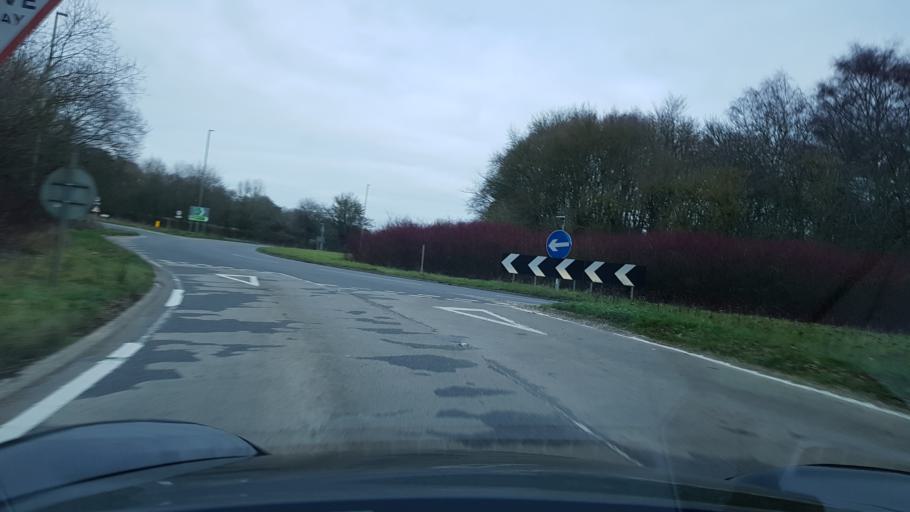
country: GB
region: England
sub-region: Hampshire
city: Alton
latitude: 51.1321
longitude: -0.9960
